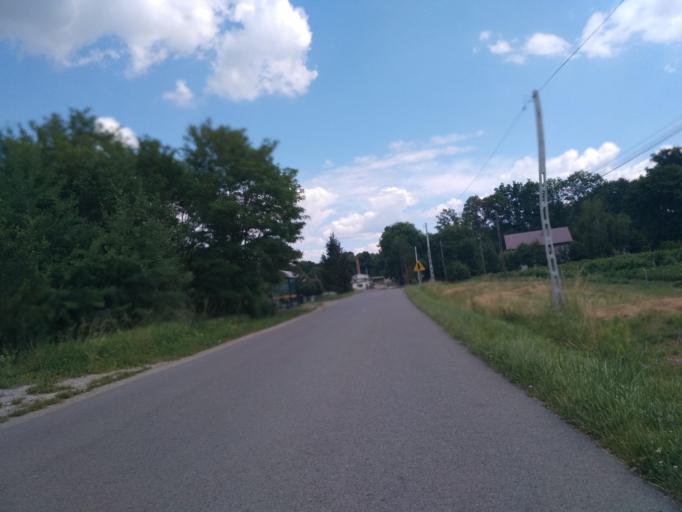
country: PL
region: Subcarpathian Voivodeship
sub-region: Powiat debicki
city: Brzostek
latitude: 49.8609
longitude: 21.4421
